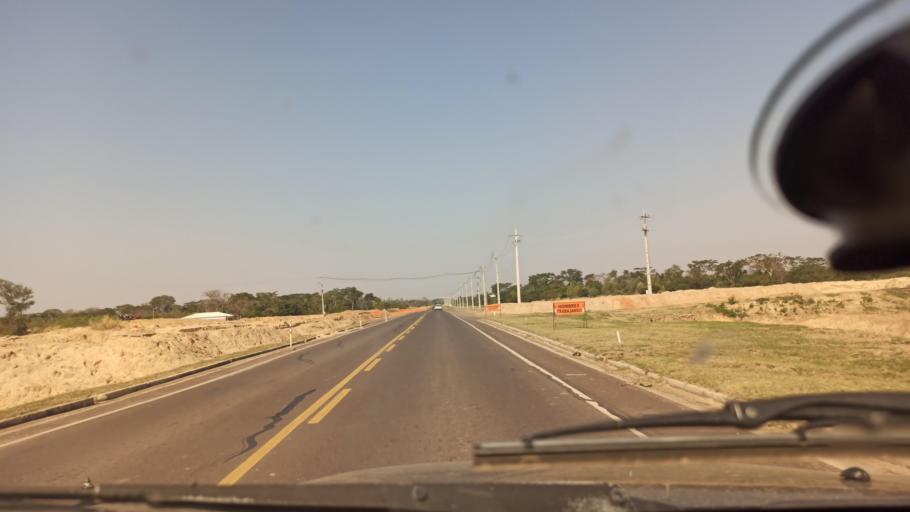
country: PY
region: Central
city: Colonia Mariano Roque Alonso
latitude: -25.1888
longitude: -57.5828
